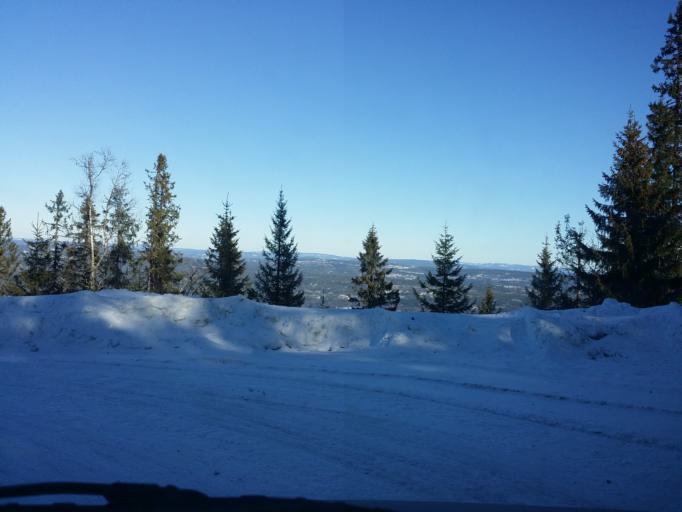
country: NO
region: Buskerud
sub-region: Ringerike
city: Honefoss
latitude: 60.3994
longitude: 10.0185
